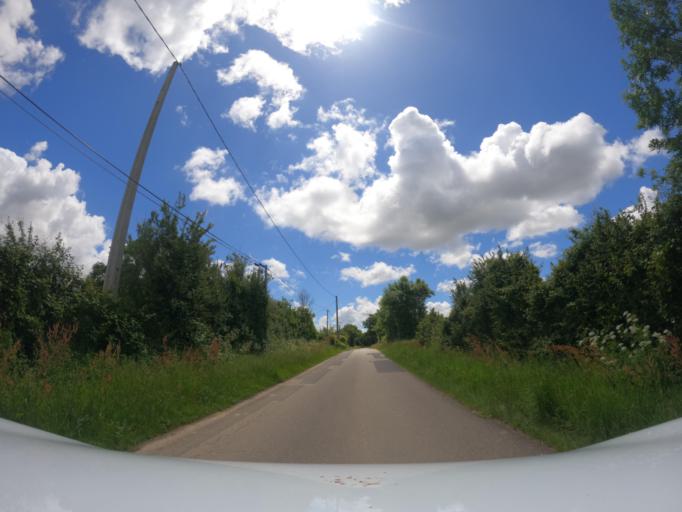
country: FR
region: Pays de la Loire
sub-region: Departement de la Vendee
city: Le Champ-Saint-Pere
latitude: 46.4906
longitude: -1.3572
